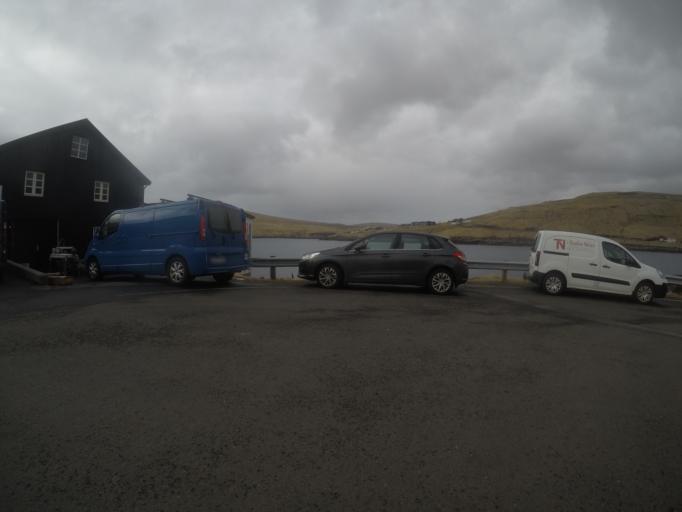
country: FO
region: Vagar
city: Midvagur
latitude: 62.0498
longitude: -7.1503
